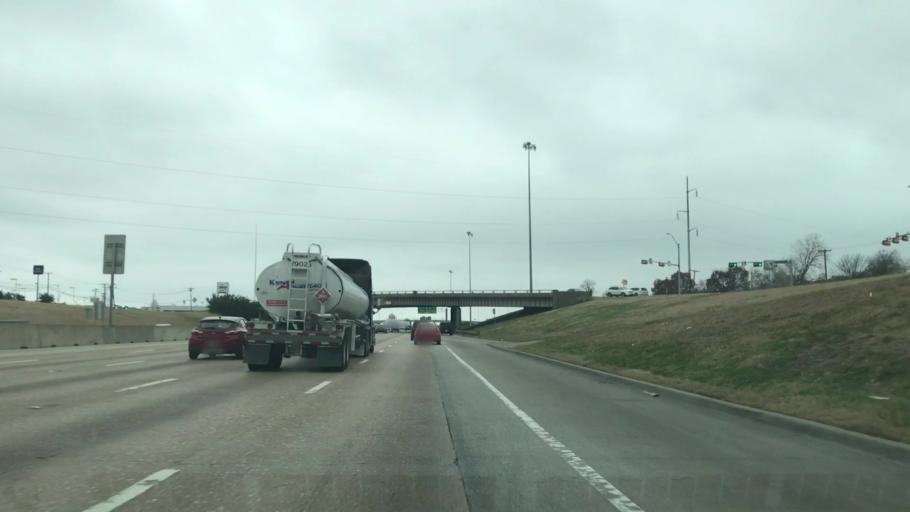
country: US
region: Texas
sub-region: Dallas County
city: Mesquite
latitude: 32.8337
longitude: -96.6322
